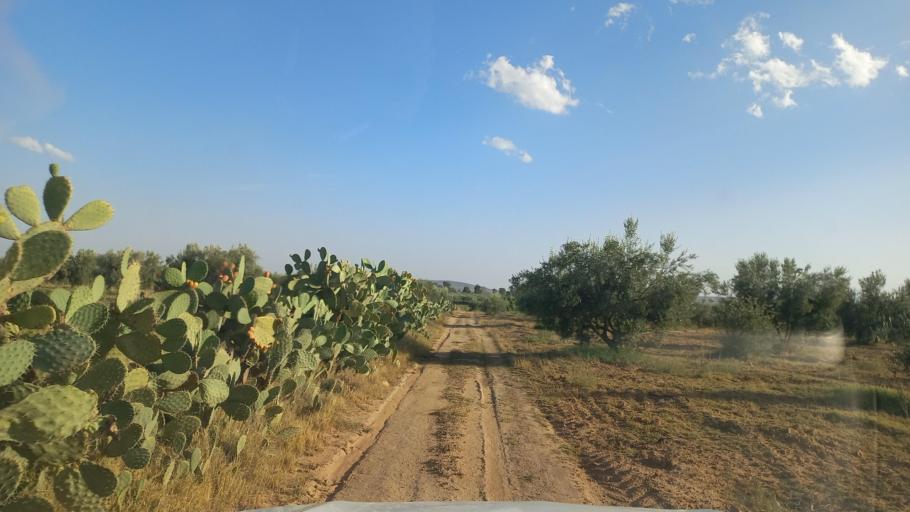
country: TN
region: Al Qasrayn
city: Kasserine
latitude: 35.2674
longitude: 9.0327
